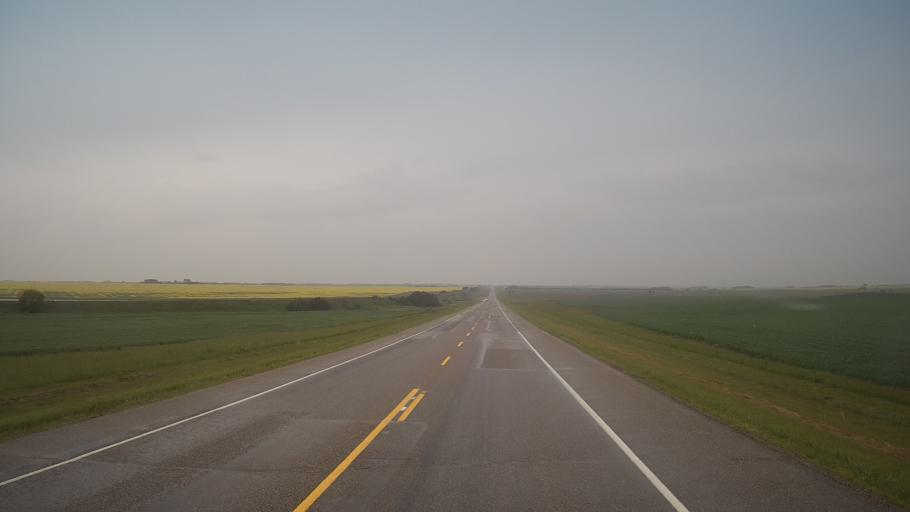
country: CA
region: Saskatchewan
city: Wilkie
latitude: 52.2105
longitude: -108.4904
